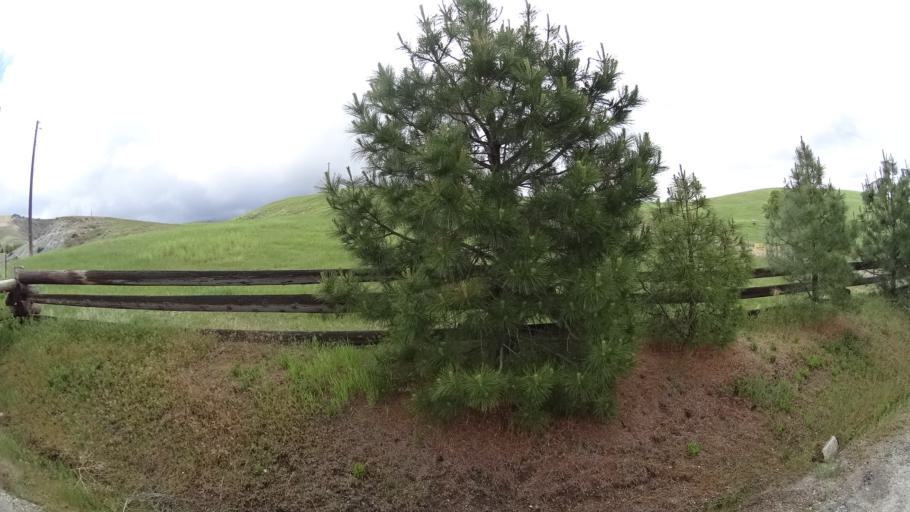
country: US
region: Idaho
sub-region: Ada County
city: Garden City
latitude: 43.7409
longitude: -116.2254
